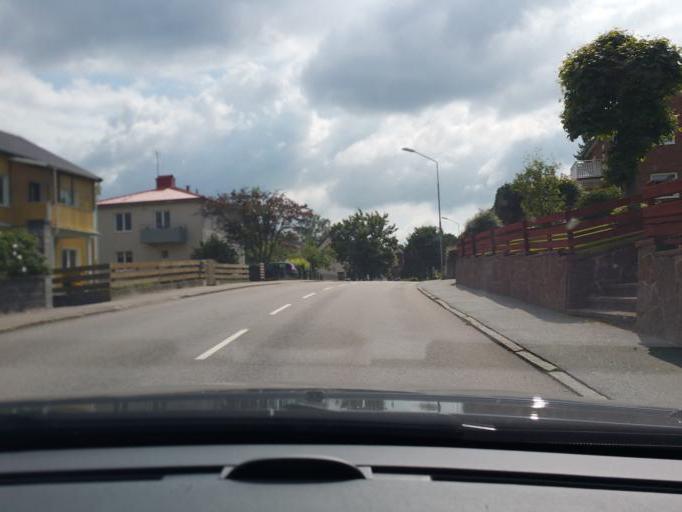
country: SE
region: Kronoberg
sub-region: Vaxjo Kommun
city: Lammhult
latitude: 57.1676
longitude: 14.5779
